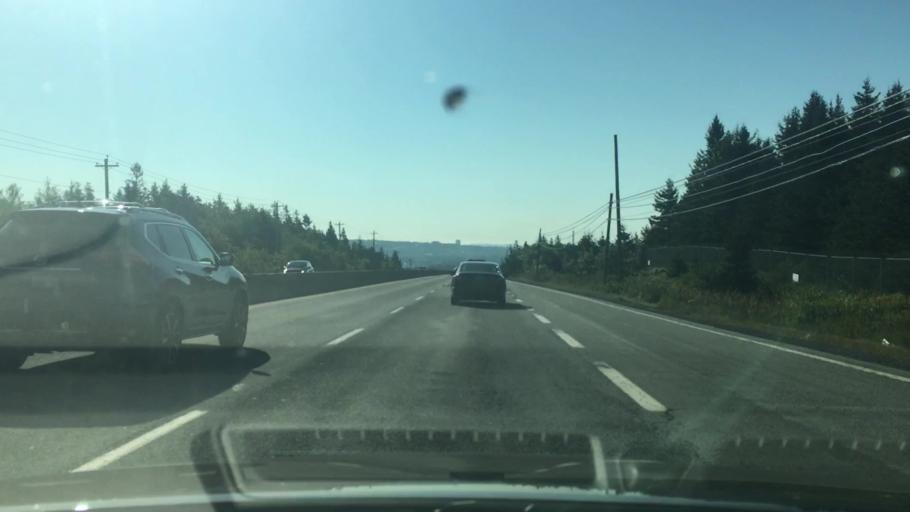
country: CA
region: Nova Scotia
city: Dartmouth
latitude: 44.7178
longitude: -63.6348
